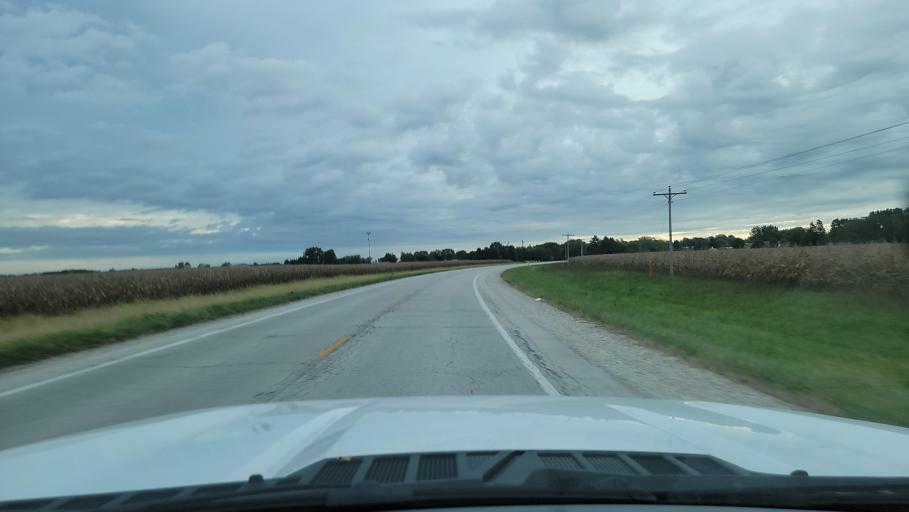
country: US
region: Illinois
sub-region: Schuyler County
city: Rushville
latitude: 40.1146
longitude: -90.5857
